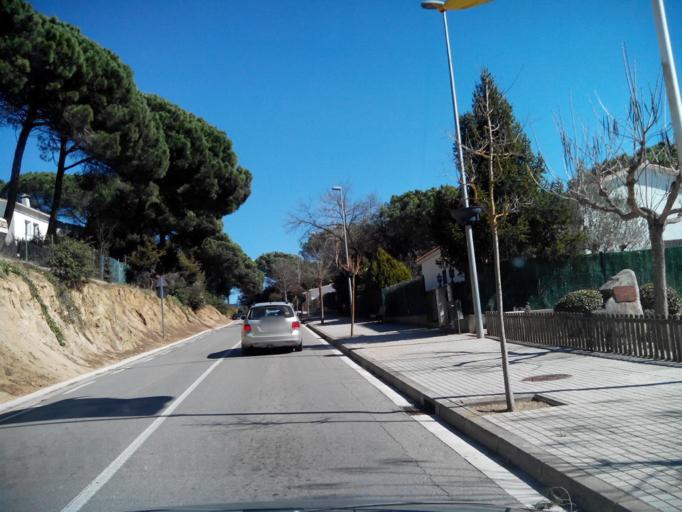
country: ES
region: Catalonia
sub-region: Provincia de Barcelona
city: Dosrius
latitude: 41.5975
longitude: 2.4398
